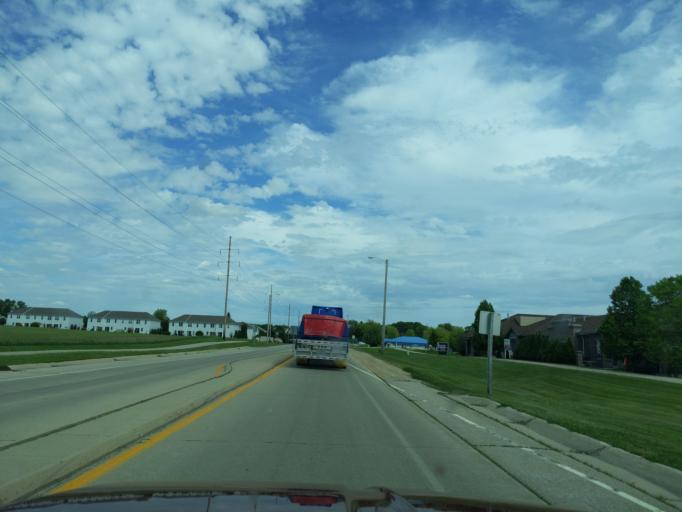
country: US
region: Wisconsin
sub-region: Dane County
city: Sun Prairie
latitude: 43.1870
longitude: -89.2595
